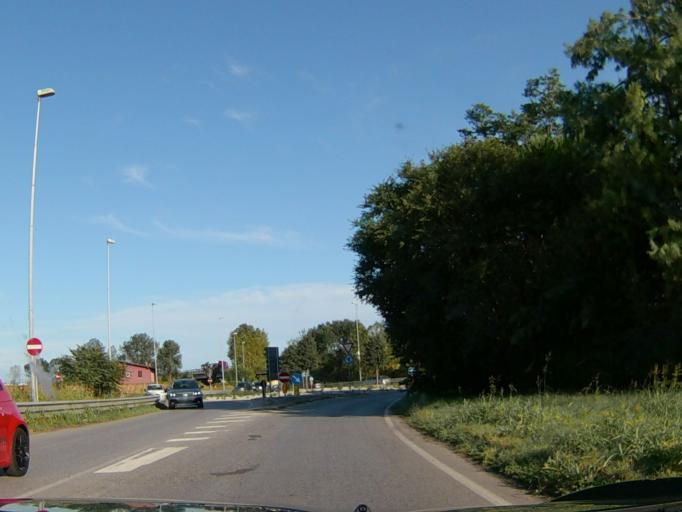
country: IT
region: Lombardy
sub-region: Provincia di Brescia
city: Molinetto
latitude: 45.4855
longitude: 10.3738
